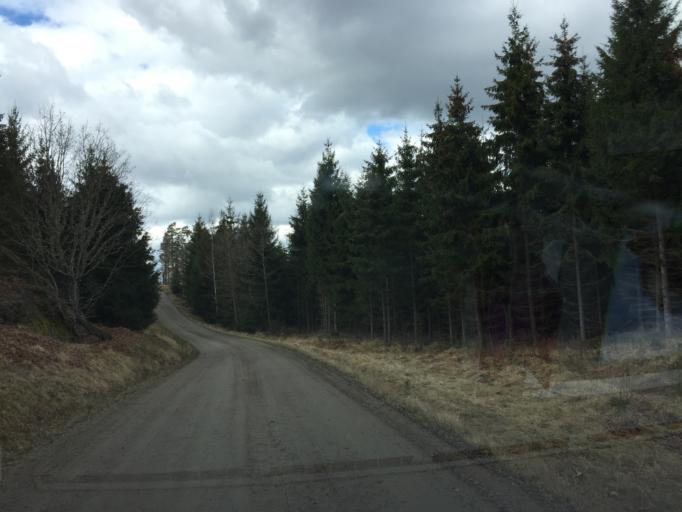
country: SE
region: Soedermanland
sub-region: Nykopings Kommun
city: Nykoping
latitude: 58.9896
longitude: 16.9769
